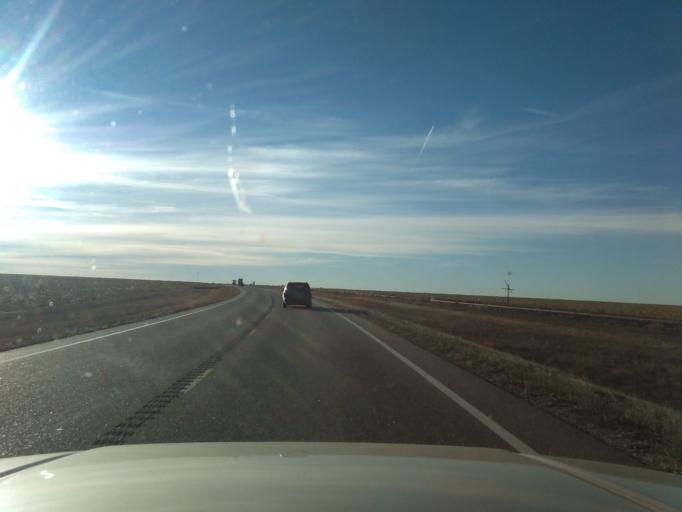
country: US
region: Kansas
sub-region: Thomas County
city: Colby
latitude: 39.4644
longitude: -100.7638
